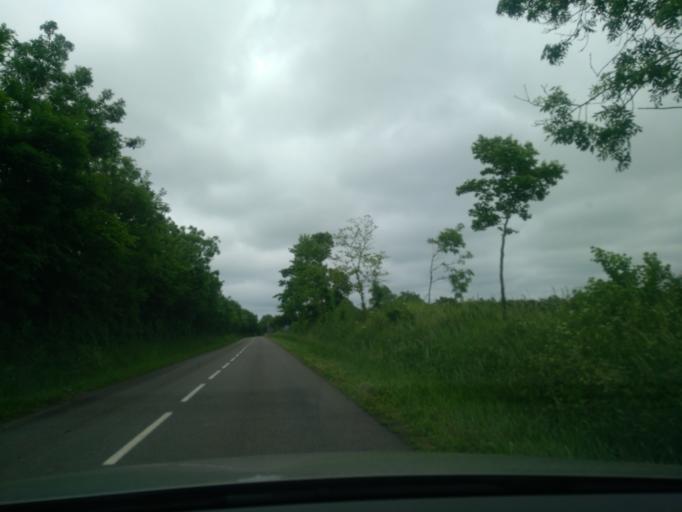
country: FR
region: Lower Normandy
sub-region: Departement de la Manche
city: Sainte-Mere-Eglise
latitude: 49.4444
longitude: -1.2853
